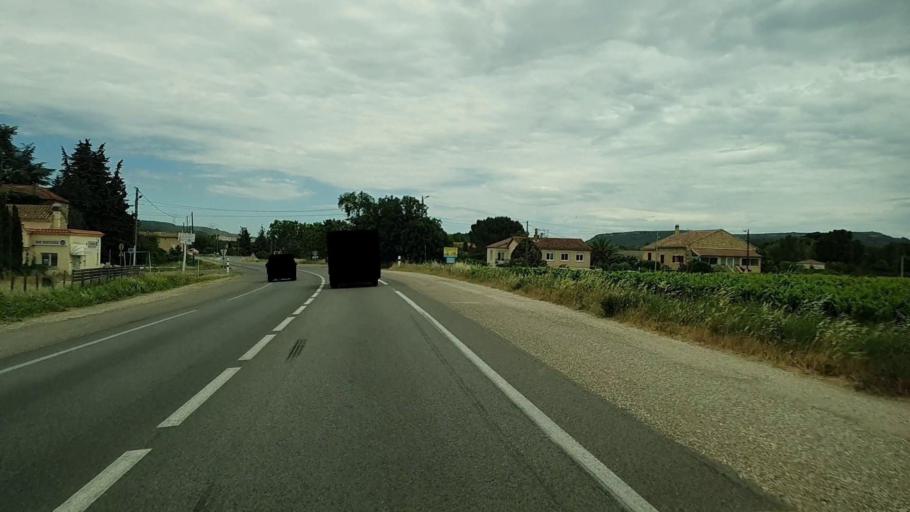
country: FR
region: Languedoc-Roussillon
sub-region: Departement du Gard
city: Connaux
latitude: 44.0913
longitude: 4.5967
